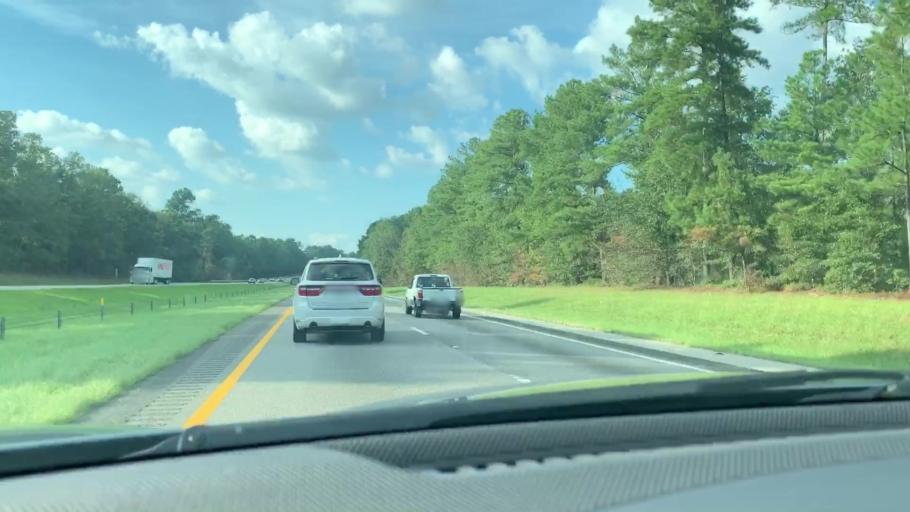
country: US
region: South Carolina
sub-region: Calhoun County
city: Oak Grove
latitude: 33.6888
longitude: -80.9089
